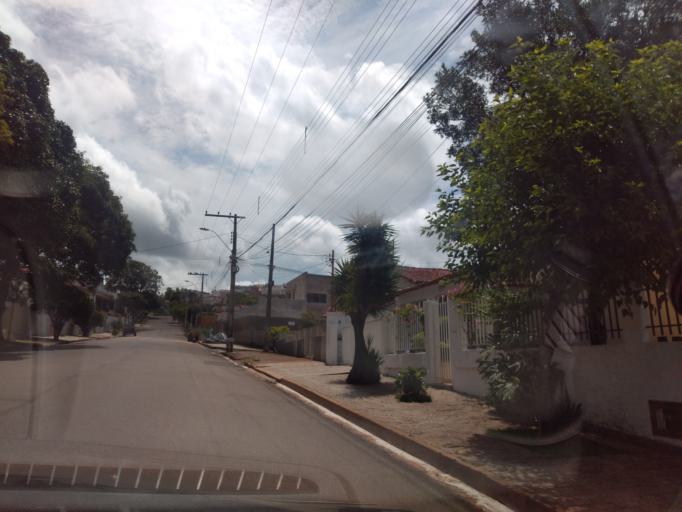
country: BR
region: Minas Gerais
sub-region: Tres Coracoes
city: Tres Coracoes
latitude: -21.6733
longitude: -45.2738
